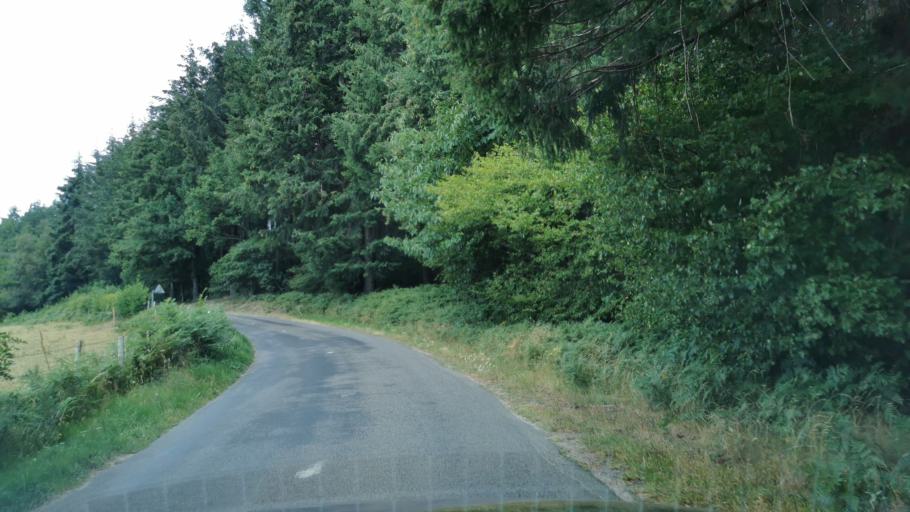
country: FR
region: Bourgogne
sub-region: Departement de Saone-et-Loire
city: Marmagne
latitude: 46.8102
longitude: 4.2849
